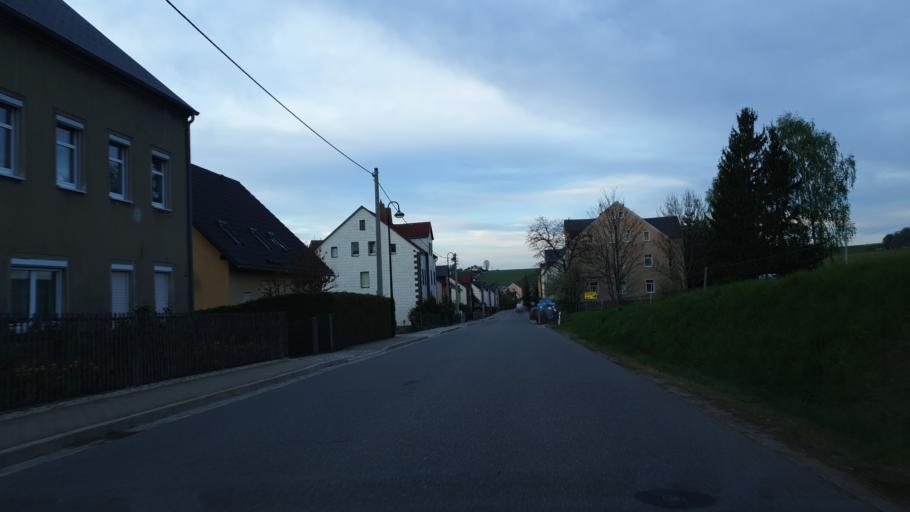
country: DE
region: Saxony
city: Gersdorf
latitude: 50.7404
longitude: 12.7174
